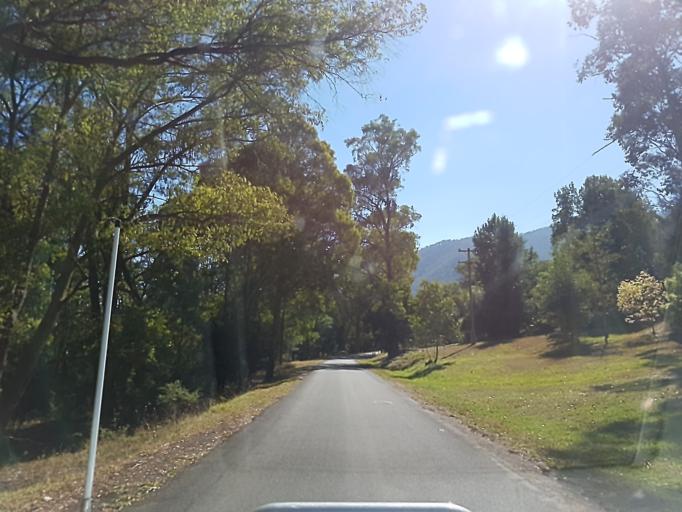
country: AU
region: Victoria
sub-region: Alpine
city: Mount Beauty
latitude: -36.8976
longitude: 147.0596
